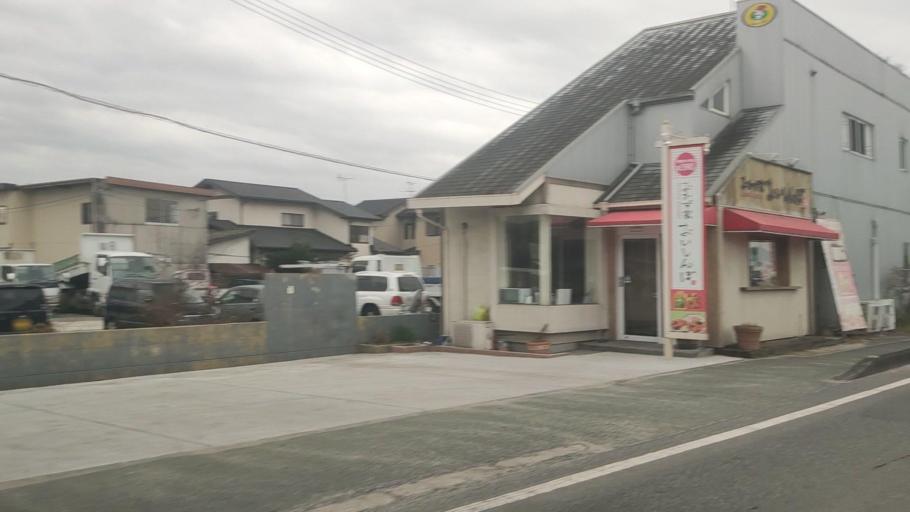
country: JP
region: Kumamoto
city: Ozu
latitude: 32.8275
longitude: 130.8014
